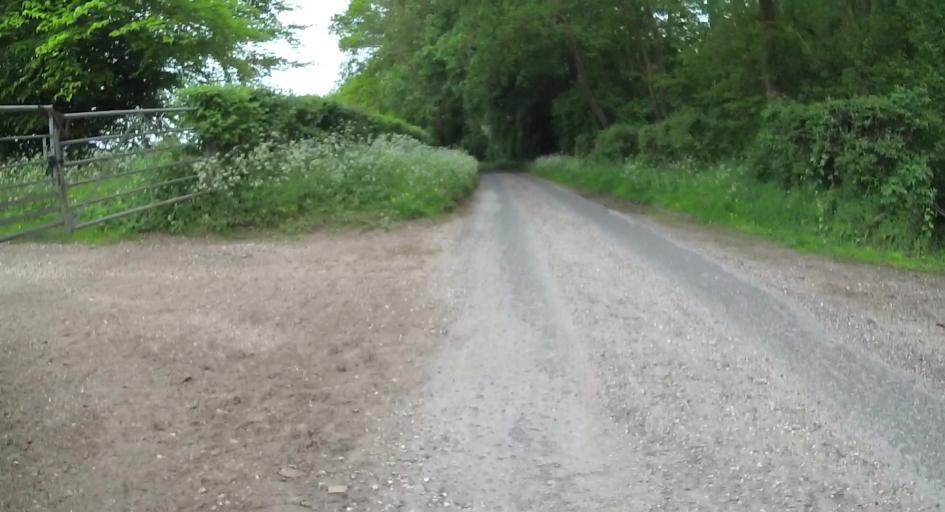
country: GB
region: England
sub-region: Hampshire
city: Overton
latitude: 51.2772
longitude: -1.2575
